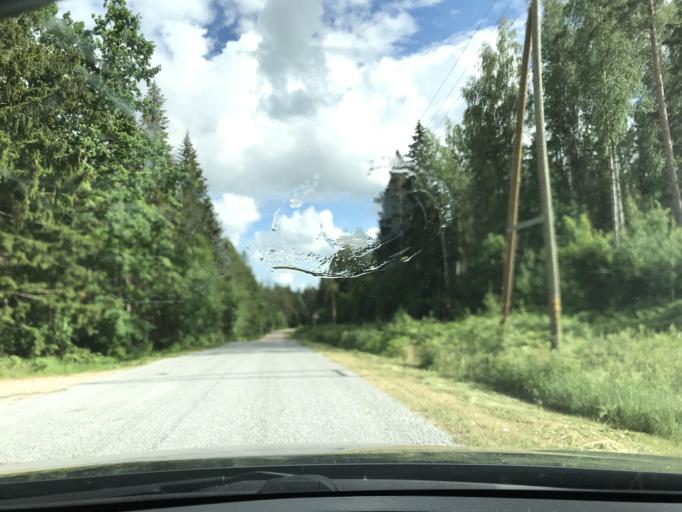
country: LV
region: Alsunga
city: Alsunga
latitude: 56.9884
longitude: 21.6286
